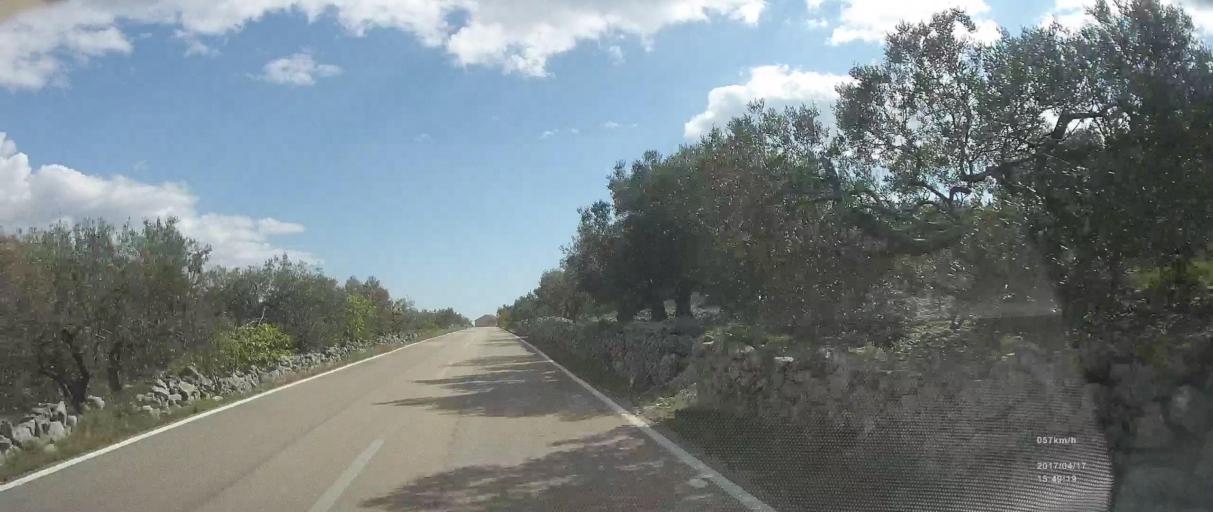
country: HR
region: Sibensko-Kniniska
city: Primosten
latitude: 43.6149
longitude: 15.9763
